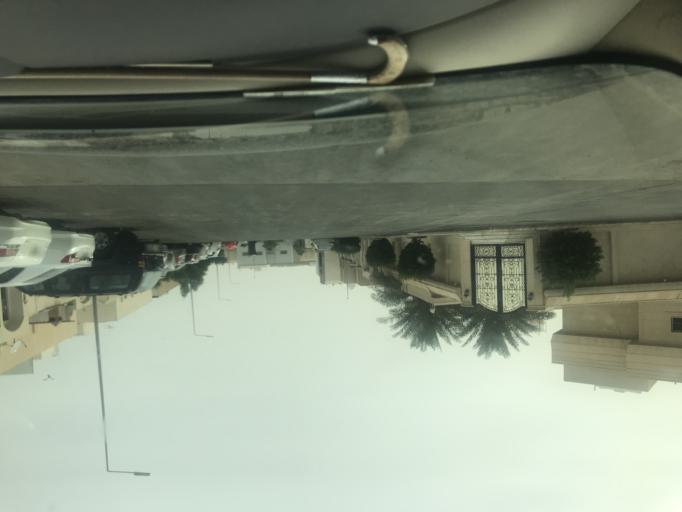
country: SA
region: Ar Riyad
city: Riyadh
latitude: 24.7344
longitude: 46.7624
